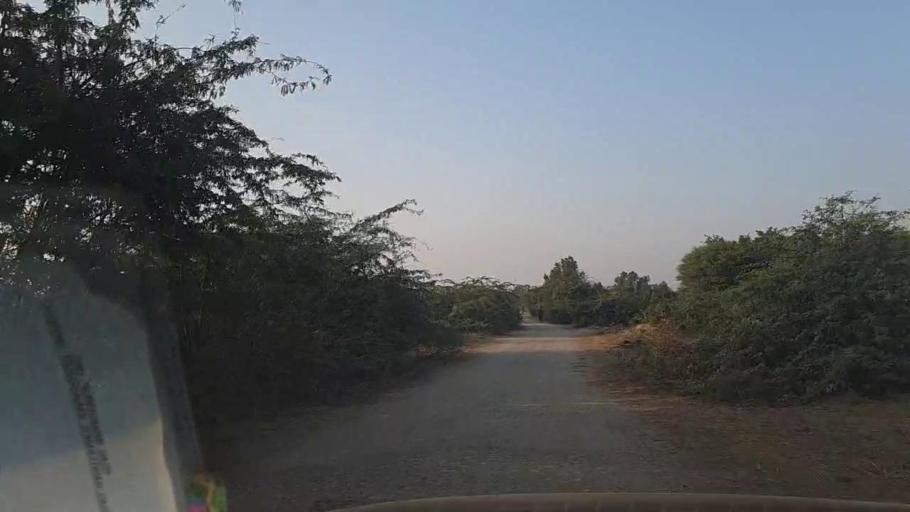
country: PK
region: Sindh
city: Keti Bandar
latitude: 24.3115
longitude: 67.6007
